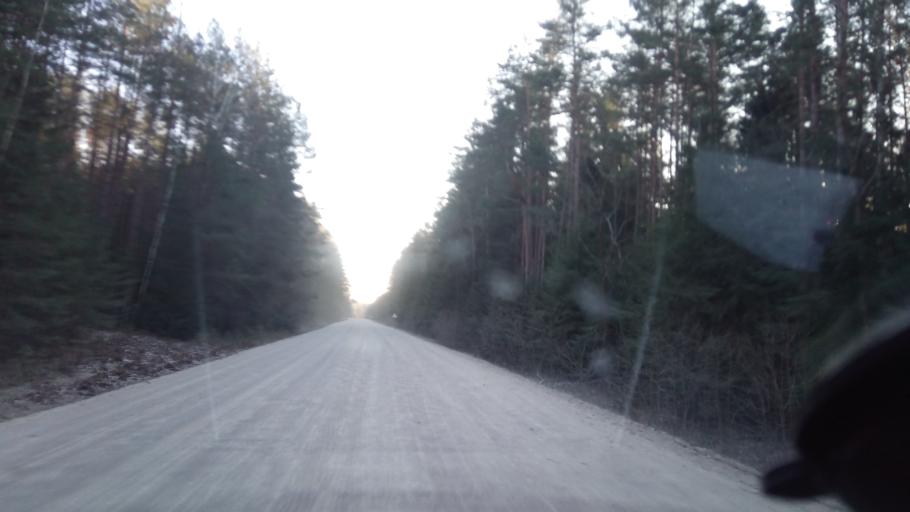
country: LT
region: Alytaus apskritis
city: Druskininkai
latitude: 54.1466
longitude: 23.9395
